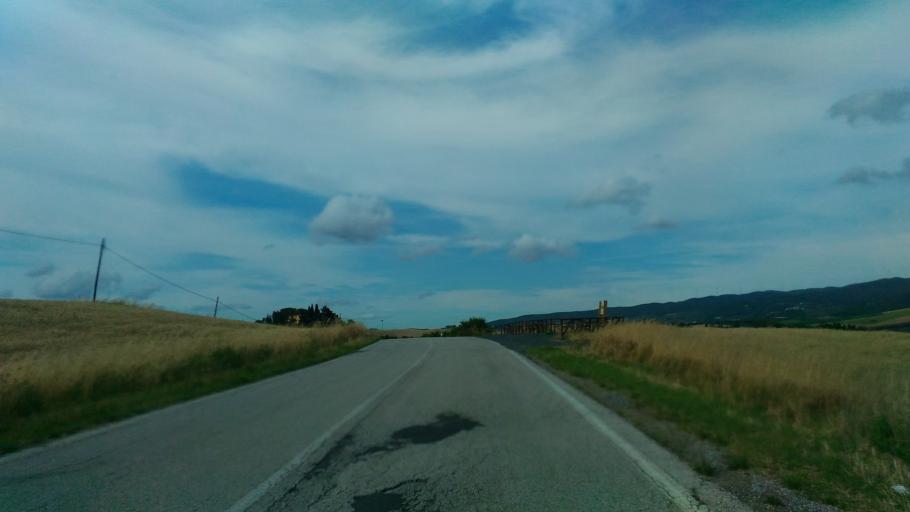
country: IT
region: Tuscany
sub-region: Province of Pisa
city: Orciano Pisano
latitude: 43.4478
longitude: 10.5110
